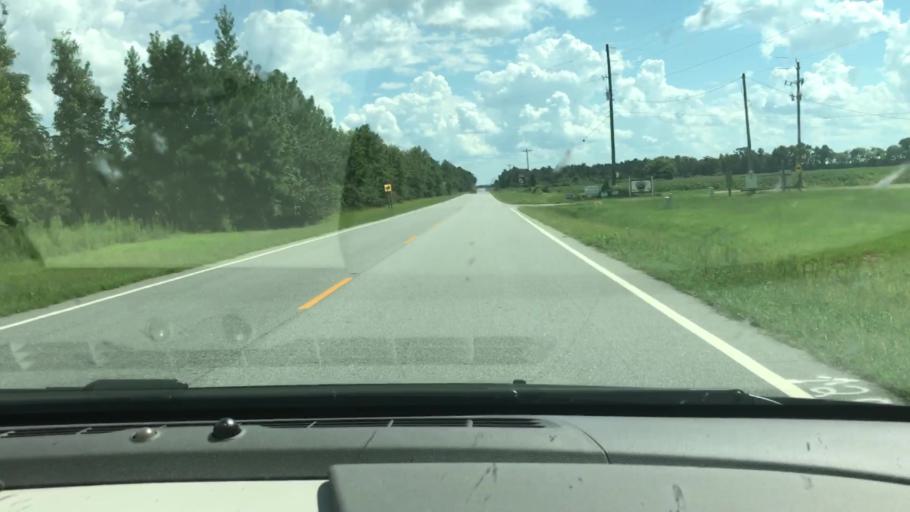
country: US
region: Georgia
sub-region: Quitman County
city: Georgetown
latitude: 31.7971
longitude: -85.0926
